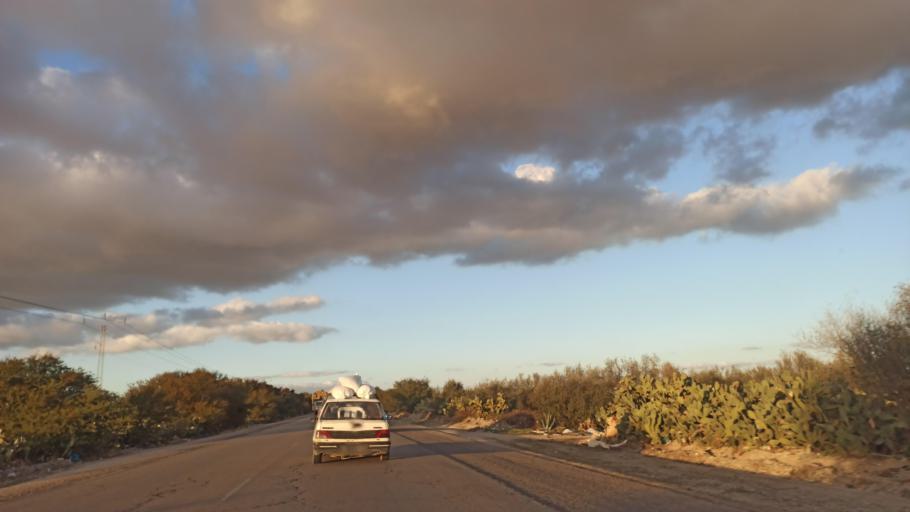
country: TN
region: Susah
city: Sidi Bou Ali
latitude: 36.0148
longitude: 10.3189
